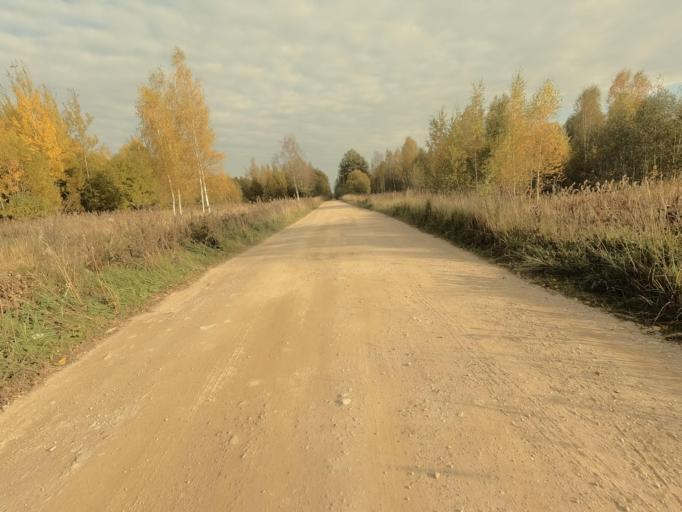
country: RU
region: Novgorod
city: Pankovka
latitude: 58.8961
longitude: 31.0058
